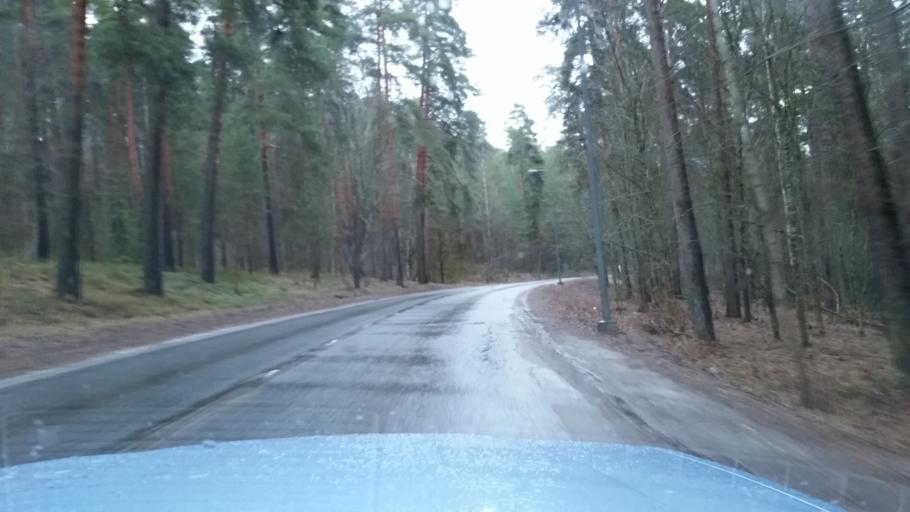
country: FI
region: Pirkanmaa
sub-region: Tampere
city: Tampere
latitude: 61.4949
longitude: 23.7324
